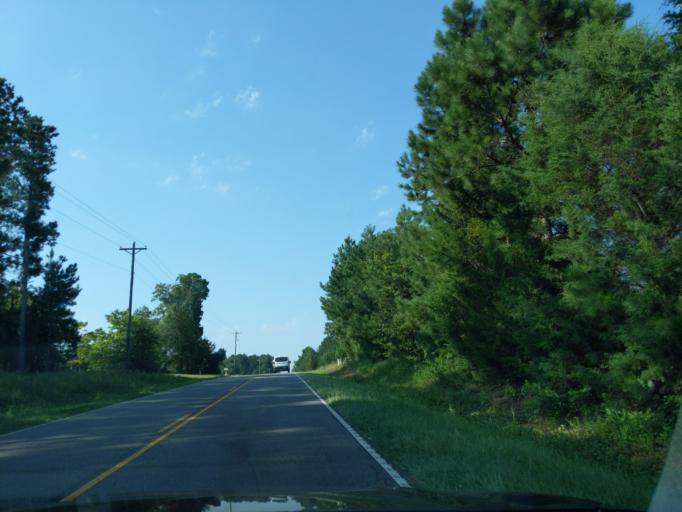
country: US
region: South Carolina
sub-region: Lexington County
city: Leesville
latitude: 33.9719
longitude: -81.5282
